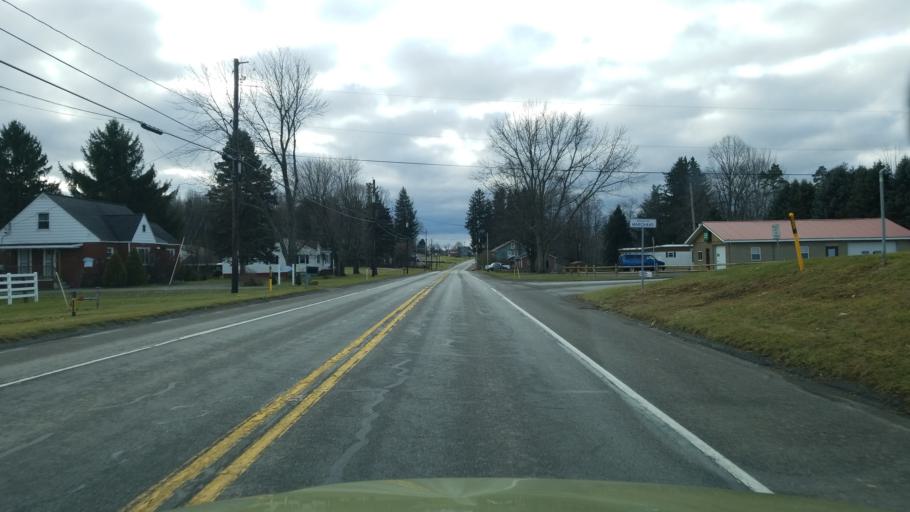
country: US
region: Pennsylvania
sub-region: Jefferson County
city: Punxsutawney
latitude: 40.8653
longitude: -79.0205
